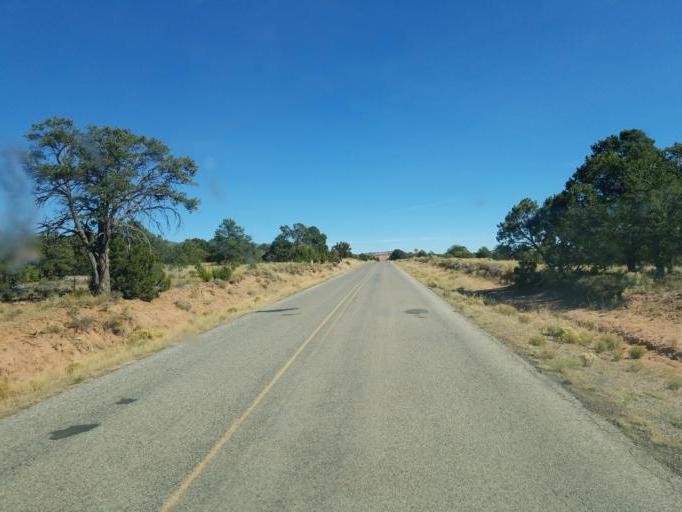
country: US
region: New Mexico
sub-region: McKinley County
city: Thoreau
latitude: 35.4373
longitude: -108.2738
